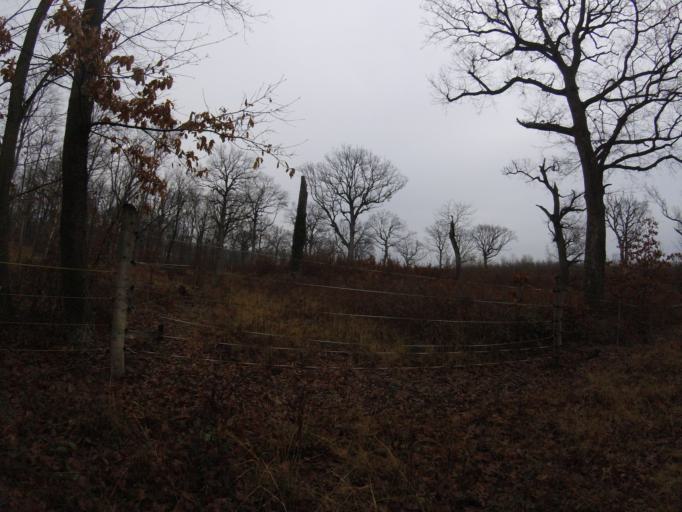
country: HU
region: Vas
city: Sarvar
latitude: 47.2334
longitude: 17.0052
